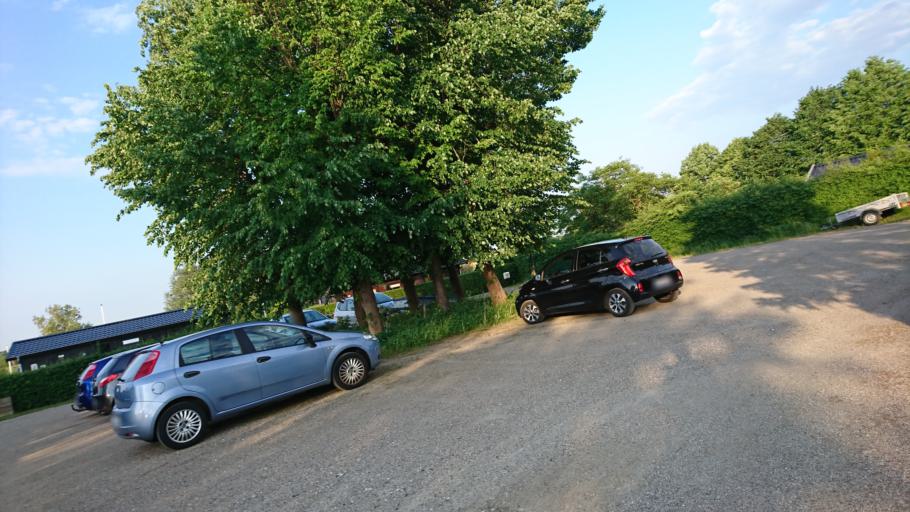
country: DK
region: Capital Region
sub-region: Egedal Kommune
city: Smorumnedre
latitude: 55.7172
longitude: 12.3287
